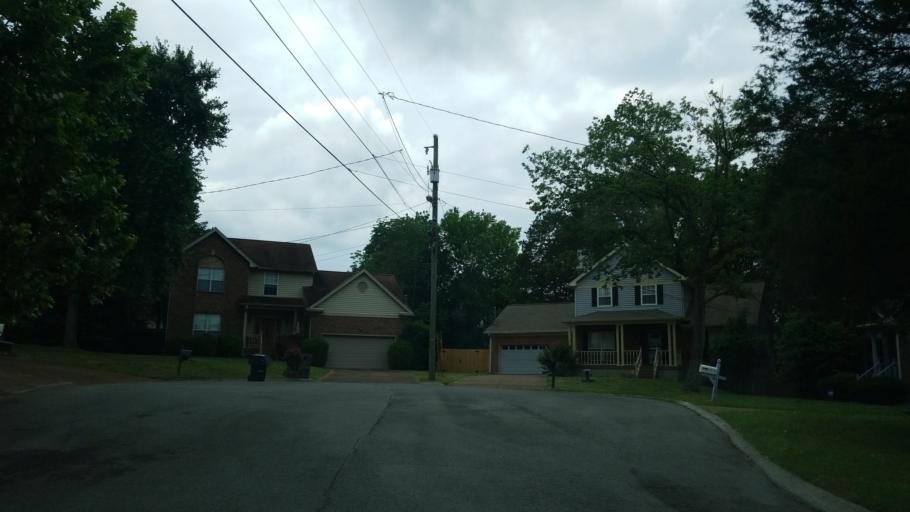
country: US
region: Tennessee
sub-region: Rutherford County
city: La Vergne
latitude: 36.0729
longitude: -86.5972
